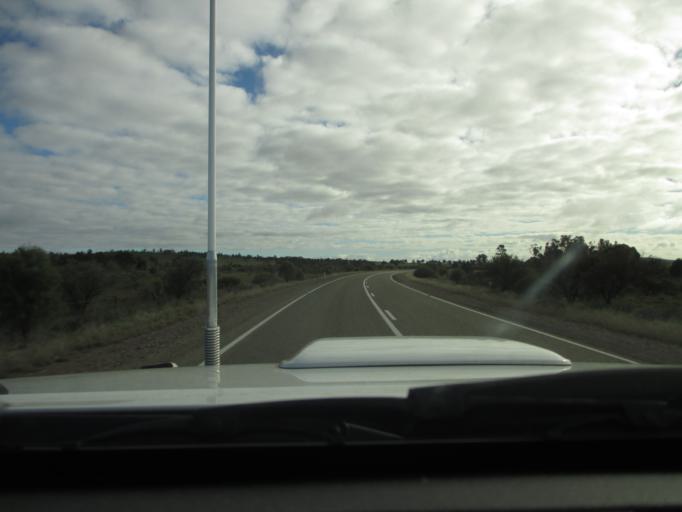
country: AU
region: South Australia
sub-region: Flinders Ranges
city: Quorn
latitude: -32.5104
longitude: 138.5464
